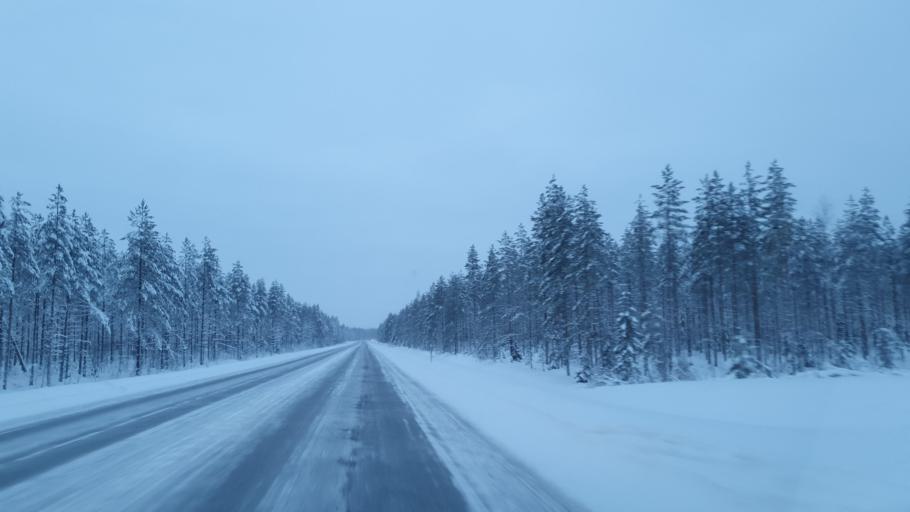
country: FI
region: Kainuu
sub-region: Kajaani
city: Vaala
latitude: 64.5979
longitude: 26.7069
